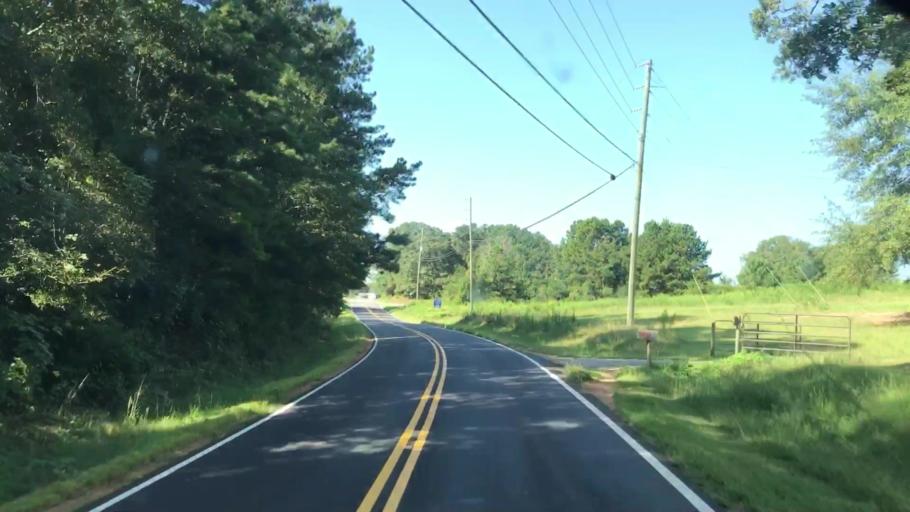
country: US
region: Georgia
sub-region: Walton County
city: Monroe
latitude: 33.8235
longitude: -83.8029
